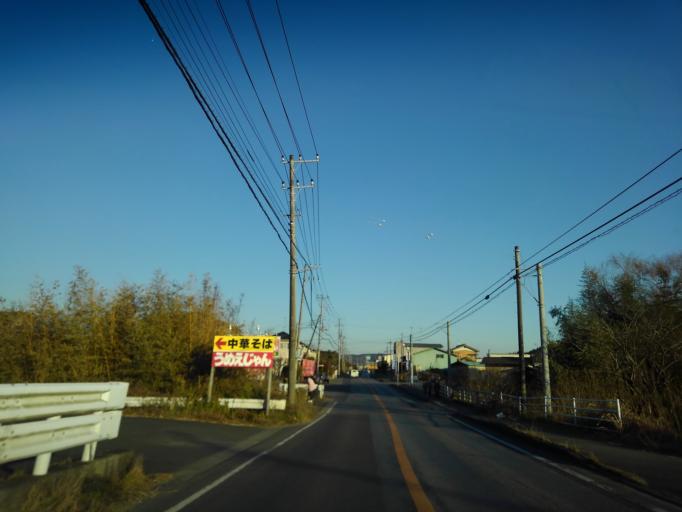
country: JP
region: Chiba
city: Kimitsu
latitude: 35.3068
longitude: 139.9499
